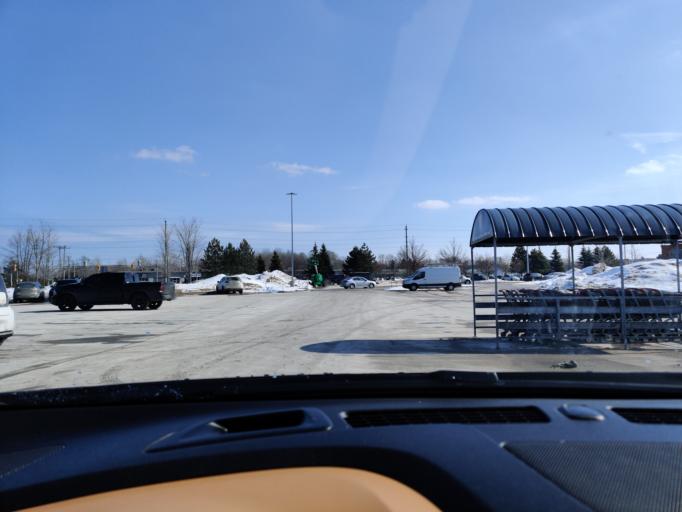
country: CA
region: Ontario
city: Collingwood
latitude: 44.5046
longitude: -80.2368
